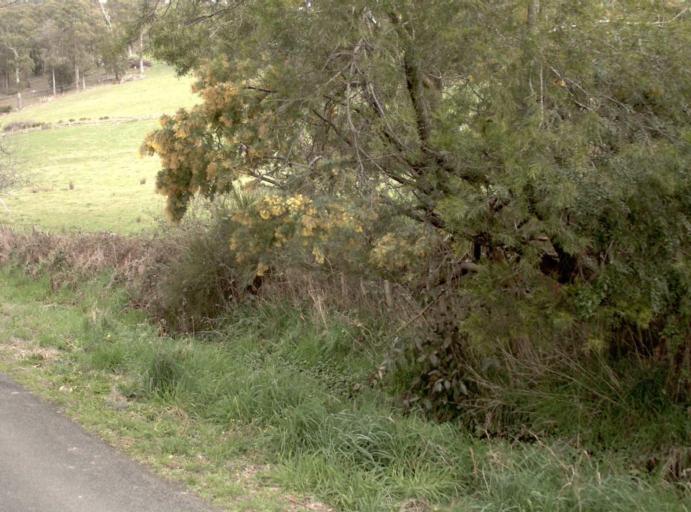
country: AU
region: Tasmania
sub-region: Launceston
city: Mayfield
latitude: -41.2651
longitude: 147.1606
